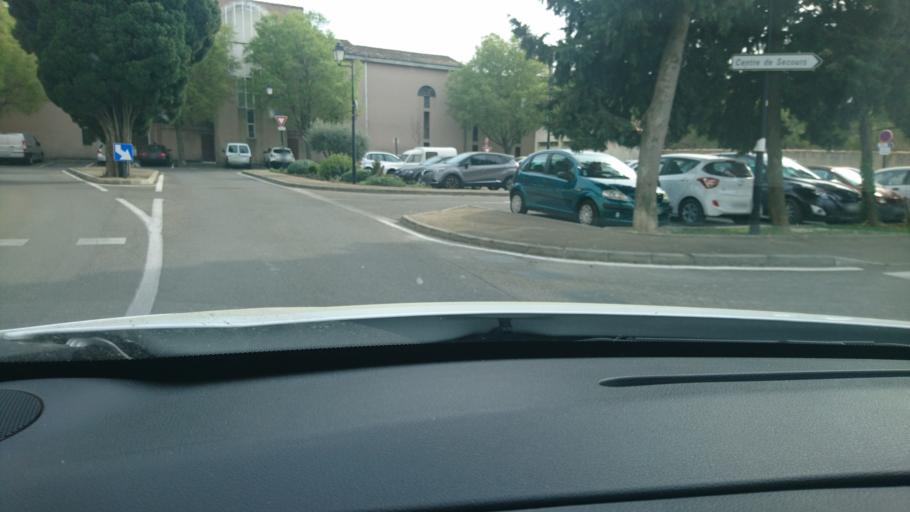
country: FR
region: Languedoc-Roussillon
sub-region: Departement du Gard
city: Villeneuve-les-Avignon
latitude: 43.9675
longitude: 4.7947
